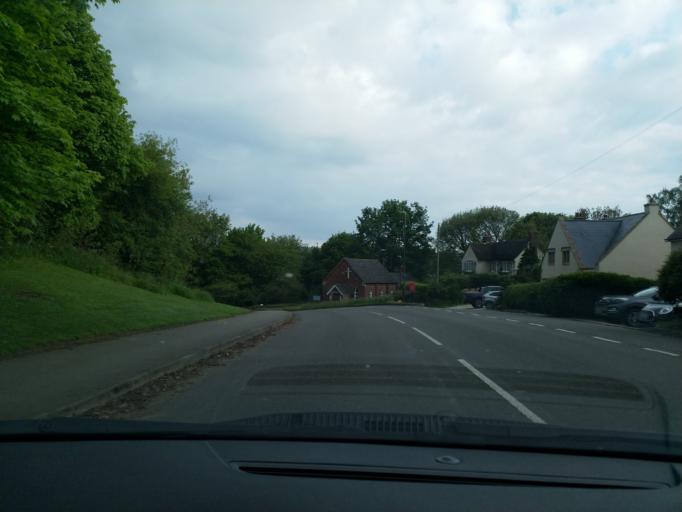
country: GB
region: England
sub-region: Derbyshire
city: Dronfield
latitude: 53.2738
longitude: -1.4909
